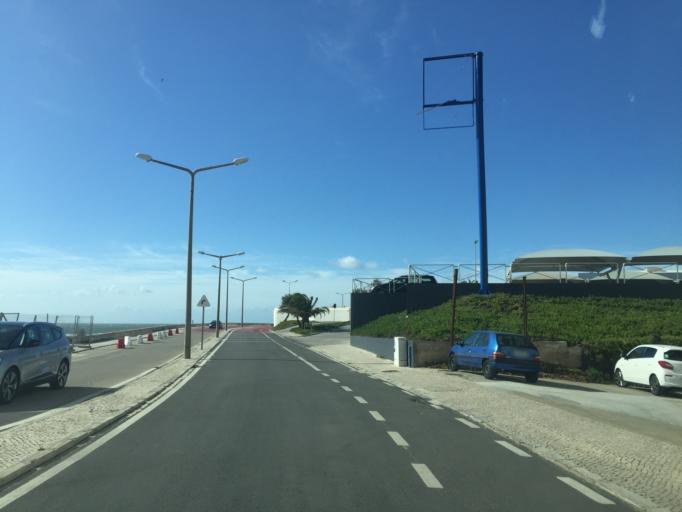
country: PT
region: Coimbra
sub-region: Figueira da Foz
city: Buarcos
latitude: 40.1667
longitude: -8.8827
